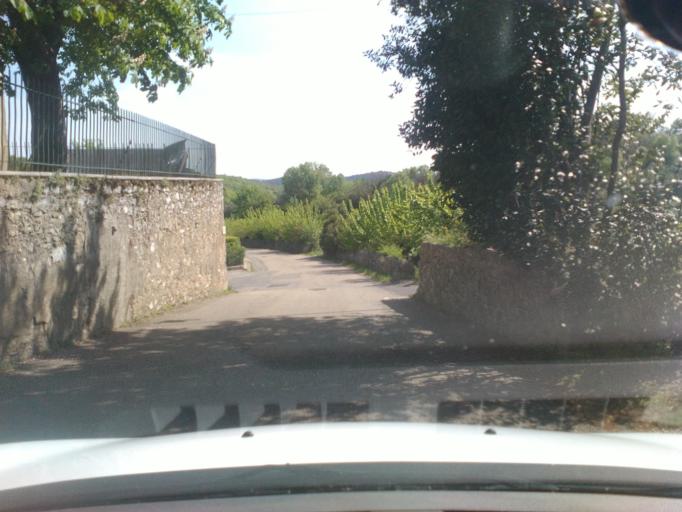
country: FR
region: Languedoc-Roussillon
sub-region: Departement du Gard
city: Saint-Hippolyte-du-Fort
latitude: 43.9999
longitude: 3.8870
